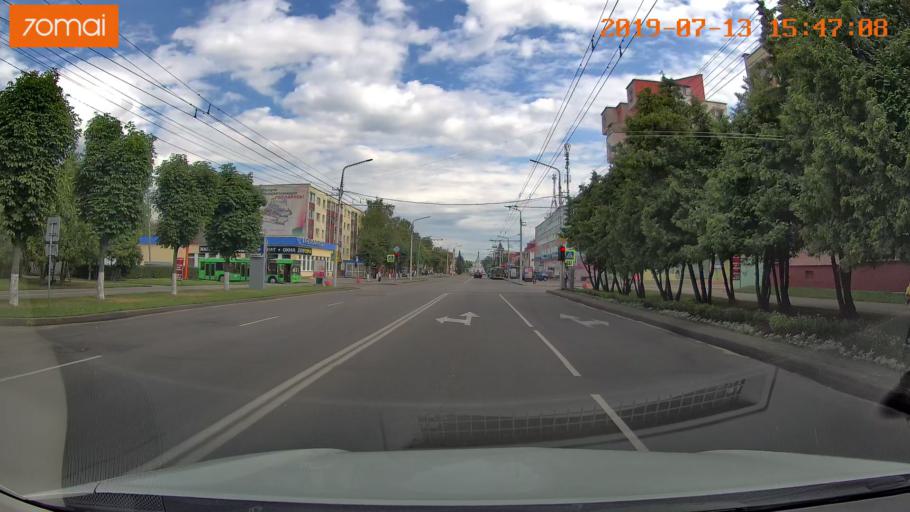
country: BY
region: Mogilev
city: Babruysk
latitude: 53.1493
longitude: 29.2287
